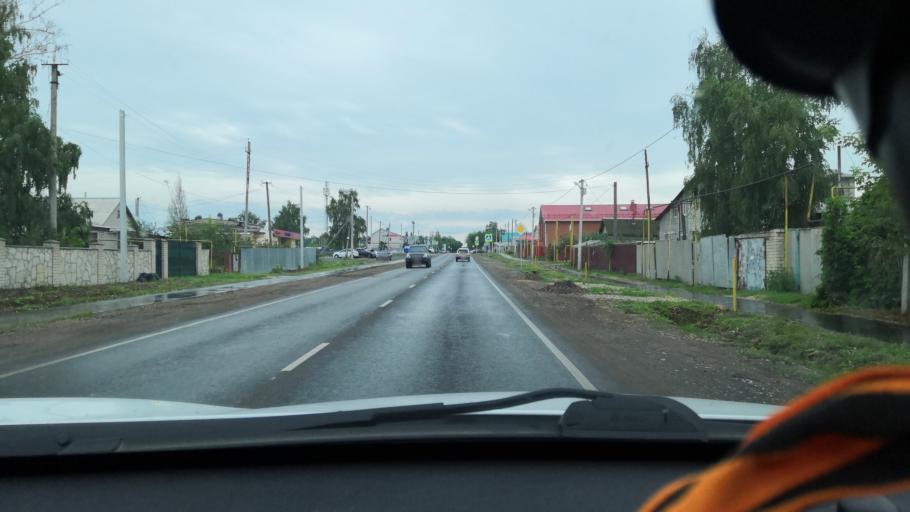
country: RU
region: Samara
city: Novosemeykino
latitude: 53.3770
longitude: 50.3454
